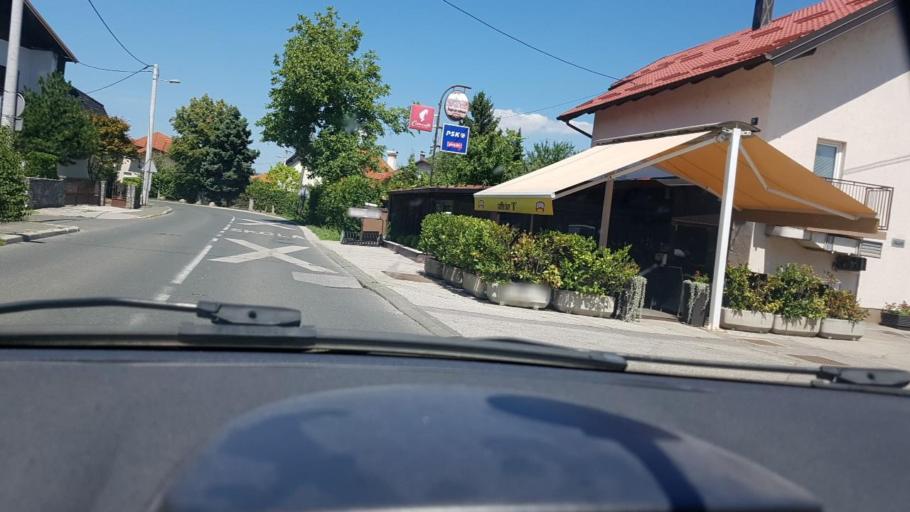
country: HR
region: Grad Zagreb
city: Brezovica
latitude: 45.7445
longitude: 15.8891
